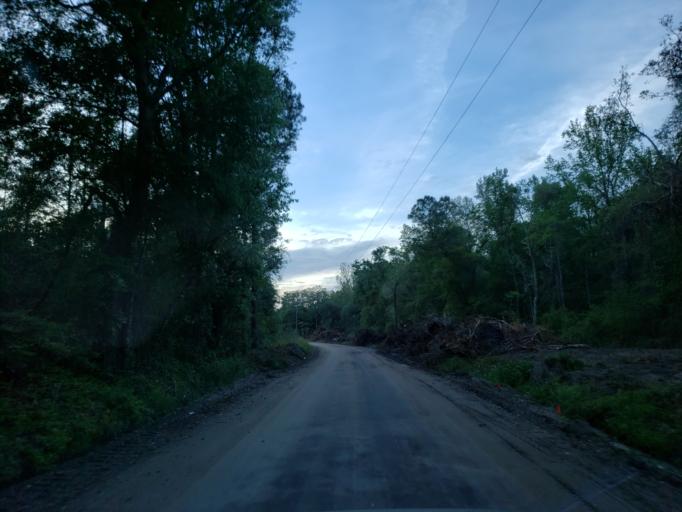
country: US
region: Georgia
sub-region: Lowndes County
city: Hahira
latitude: 30.9538
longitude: -83.3913
